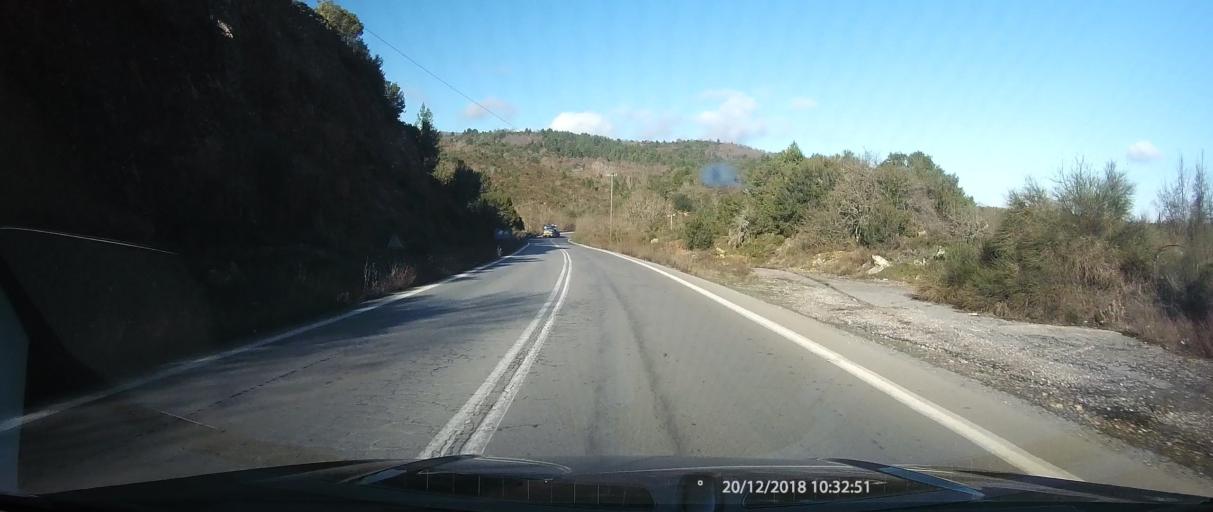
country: GR
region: Peloponnese
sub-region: Nomos Lakonias
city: Kariai
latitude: 37.3317
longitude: 22.4200
